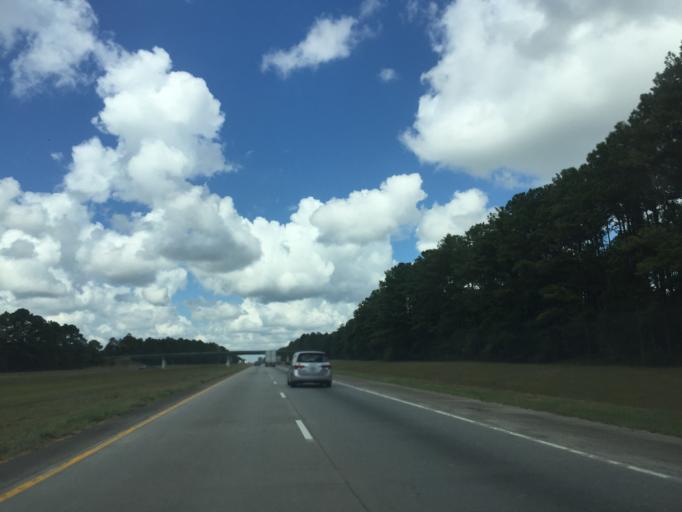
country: US
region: Georgia
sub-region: Toombs County
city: Lyons
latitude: 32.3875
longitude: -82.2643
